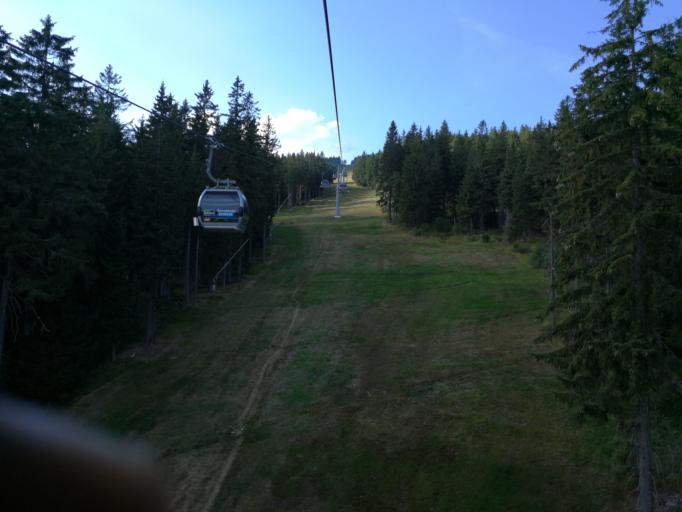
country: CZ
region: Kralovehradecky
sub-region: Okres Trutnov
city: Rudnik
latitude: 50.6368
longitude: 15.7644
